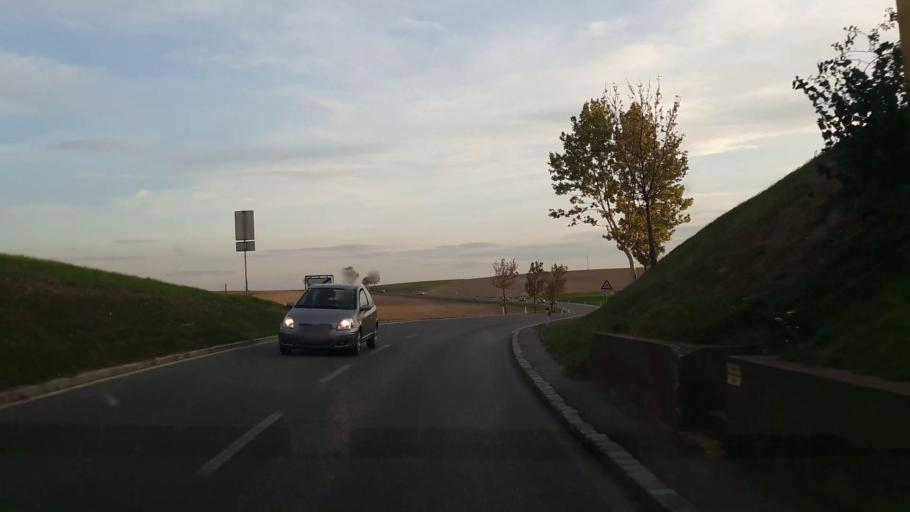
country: AT
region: Lower Austria
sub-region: Politischer Bezirk Korneuburg
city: Grossrussbach
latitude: 48.4578
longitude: 16.3733
